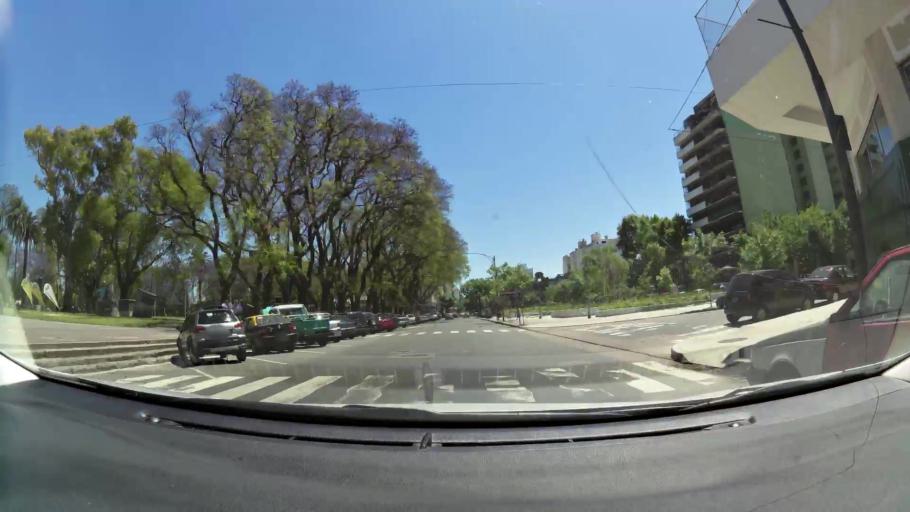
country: AR
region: Buenos Aires F.D.
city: Buenos Aires
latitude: -34.6385
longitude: -58.4053
